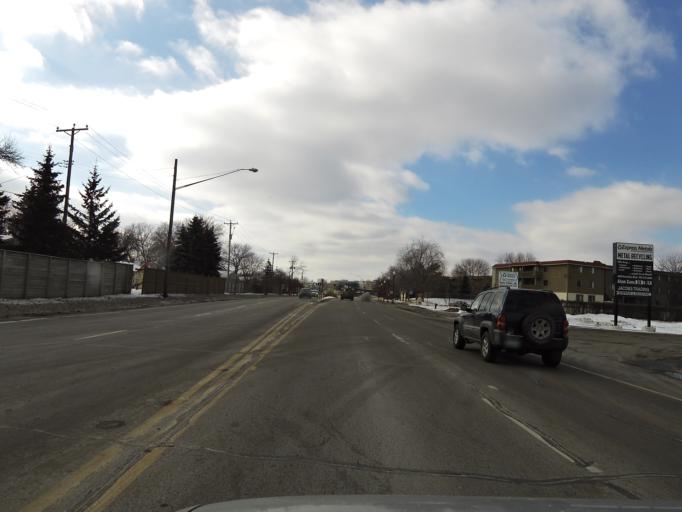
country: US
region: Minnesota
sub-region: Hennepin County
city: Saint Louis Park
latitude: 44.9259
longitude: -93.3823
